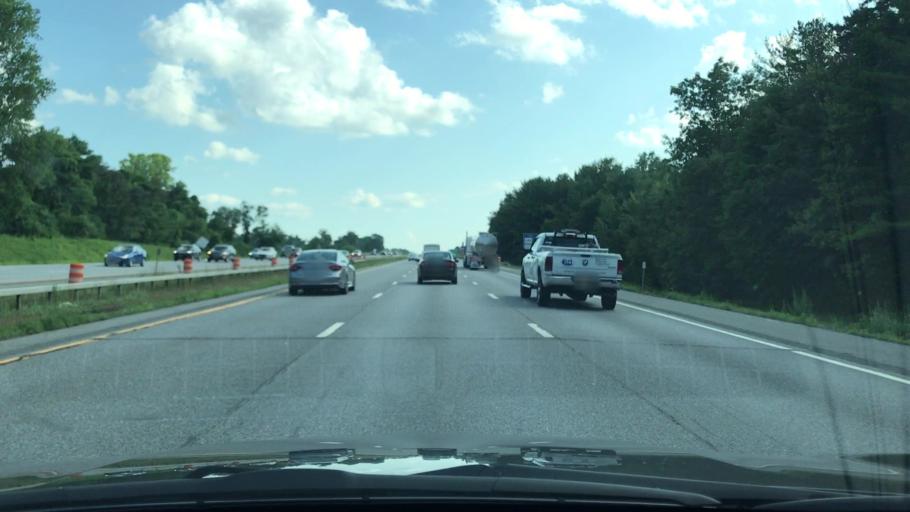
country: US
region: New York
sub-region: Warren County
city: West Glens Falls
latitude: 43.3070
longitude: -73.6766
